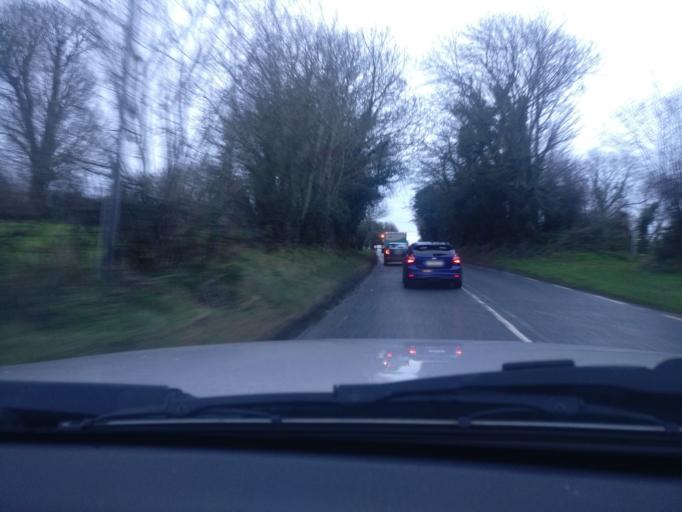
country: IE
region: Leinster
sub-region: An Mhi
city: Kells
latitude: 53.7117
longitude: -6.8173
